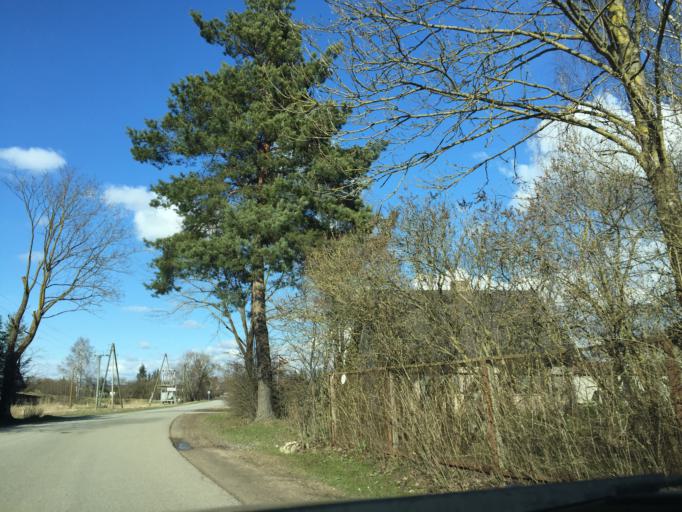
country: LV
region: Kekava
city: Kekava
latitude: 56.8401
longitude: 24.2109
